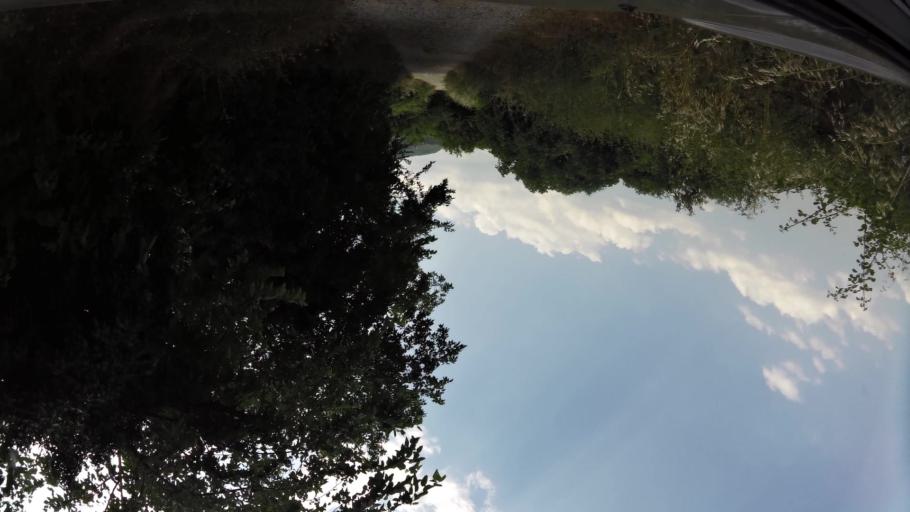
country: GR
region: Central Macedonia
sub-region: Nomos Imathias
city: Veroia
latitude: 40.5169
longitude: 22.2099
